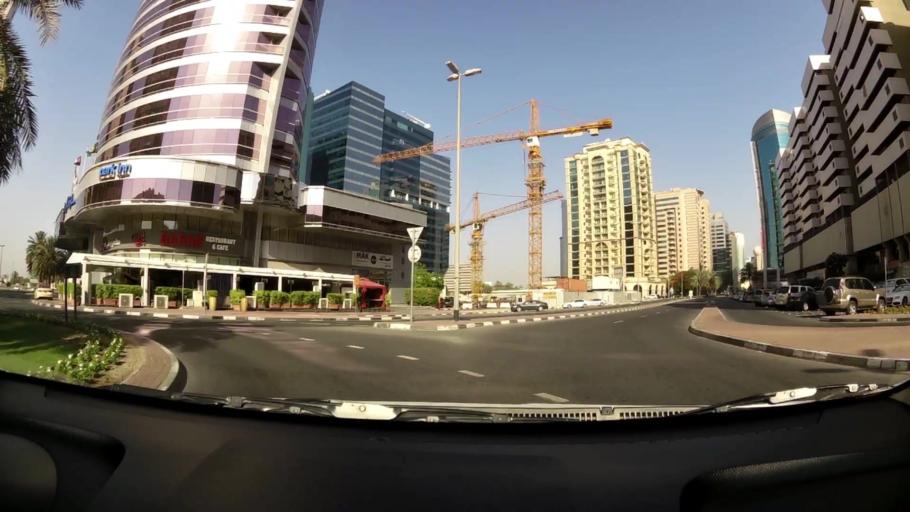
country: AE
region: Ash Shariqah
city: Sharjah
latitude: 25.2590
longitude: 55.3229
